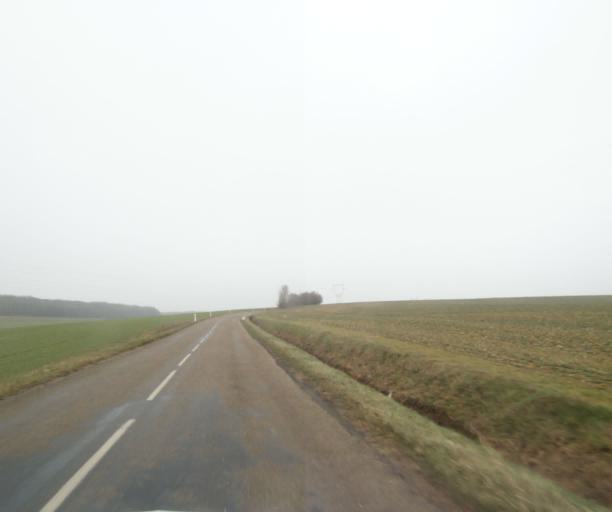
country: FR
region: Champagne-Ardenne
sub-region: Departement de la Haute-Marne
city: Bienville
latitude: 48.5153
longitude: 5.0141
